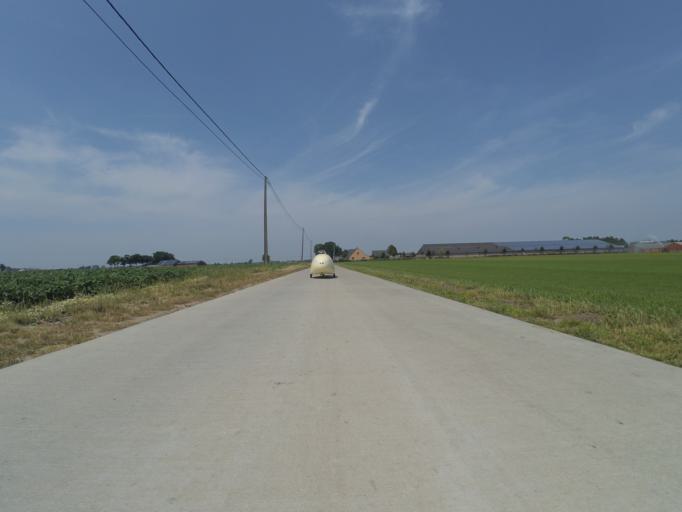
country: NL
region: North Brabant
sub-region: Gemeente Zundert
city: Zundert
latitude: 51.4173
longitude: 4.6932
